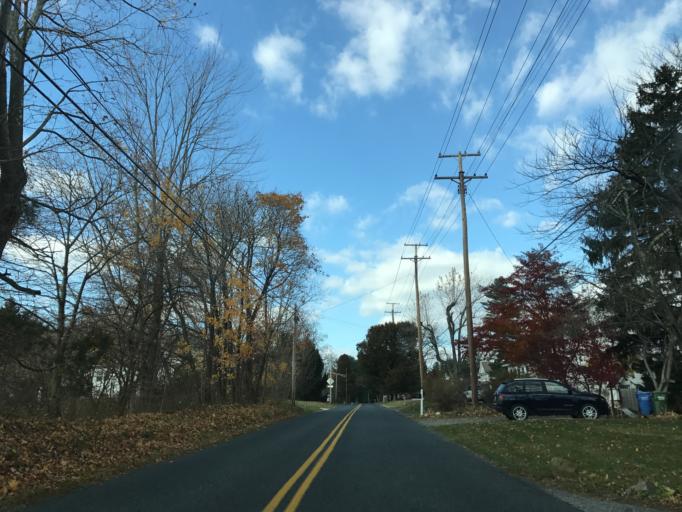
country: US
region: Maryland
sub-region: Harford County
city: Fallston
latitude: 39.5154
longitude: -76.4117
